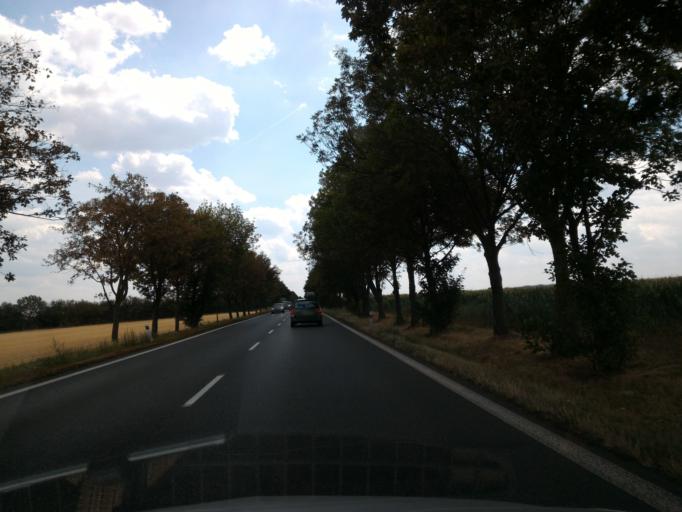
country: CZ
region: Vysocina
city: Golcuv Jenikov
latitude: 49.8529
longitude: 15.4528
